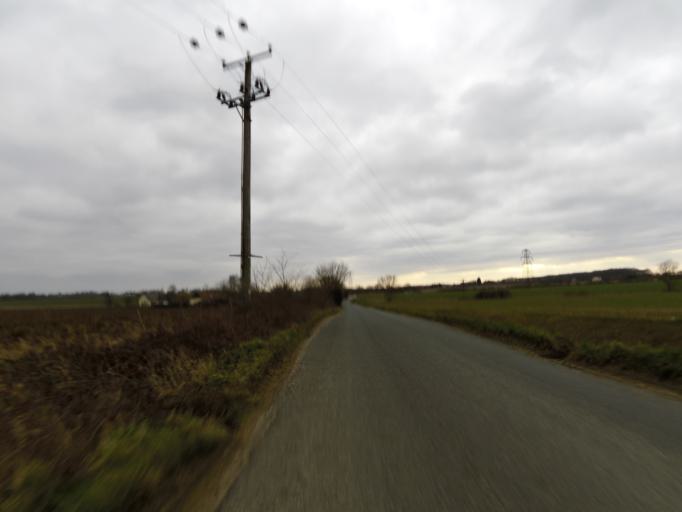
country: GB
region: England
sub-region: Suffolk
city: Ipswich
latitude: 52.1308
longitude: 1.1540
